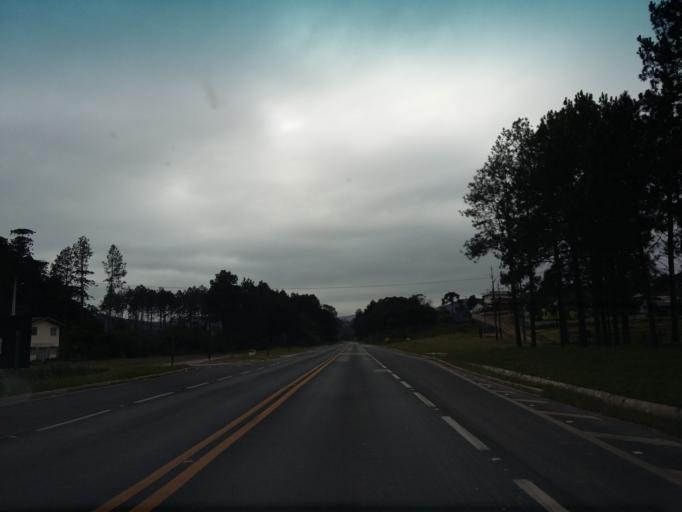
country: BR
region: Santa Catarina
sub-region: Santa Cecilia
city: Santa Cecilia
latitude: -26.7150
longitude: -50.2997
